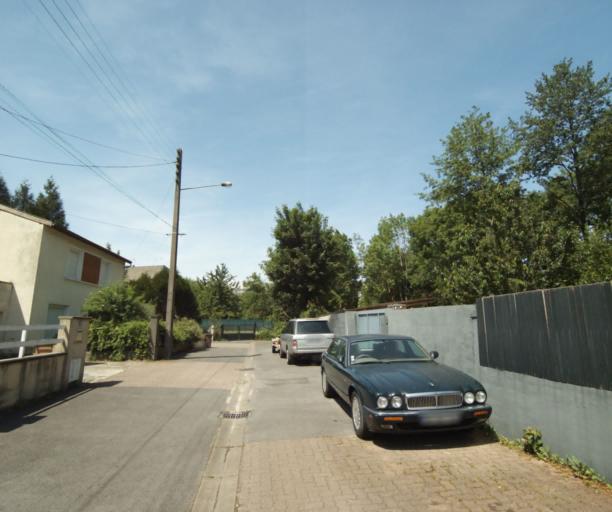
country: FR
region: Champagne-Ardenne
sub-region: Departement des Ardennes
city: Charleville-Mezieres
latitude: 49.7647
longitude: 4.7237
